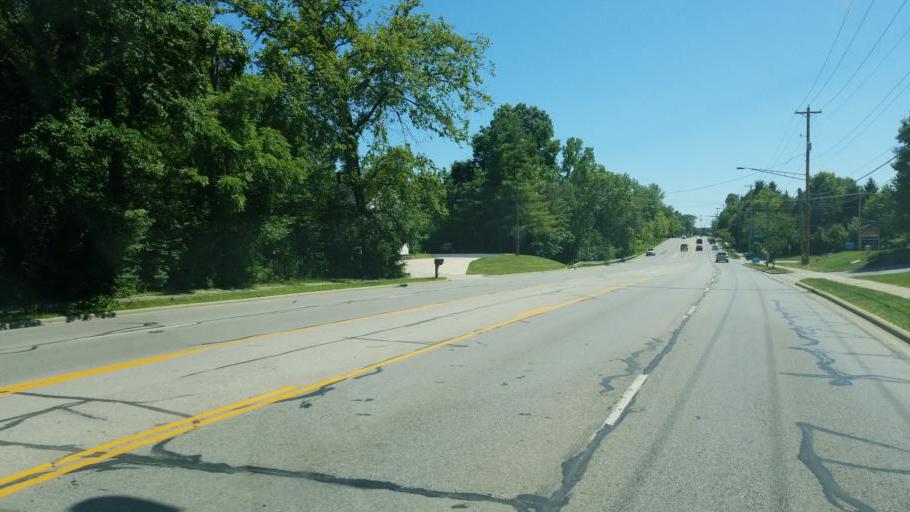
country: US
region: Ohio
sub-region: Franklin County
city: Huber Ridge
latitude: 40.0953
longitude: -82.8915
